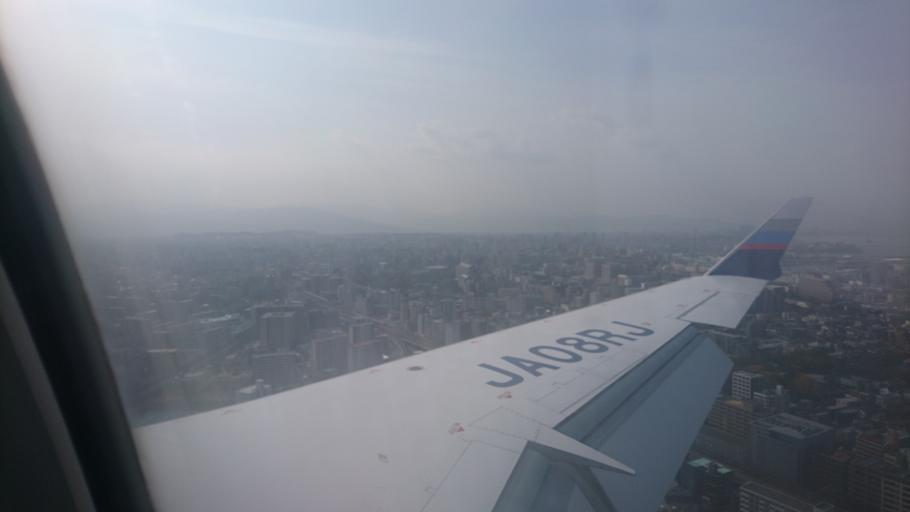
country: JP
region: Fukuoka
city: Fukuoka-shi
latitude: 33.6160
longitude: 130.4298
